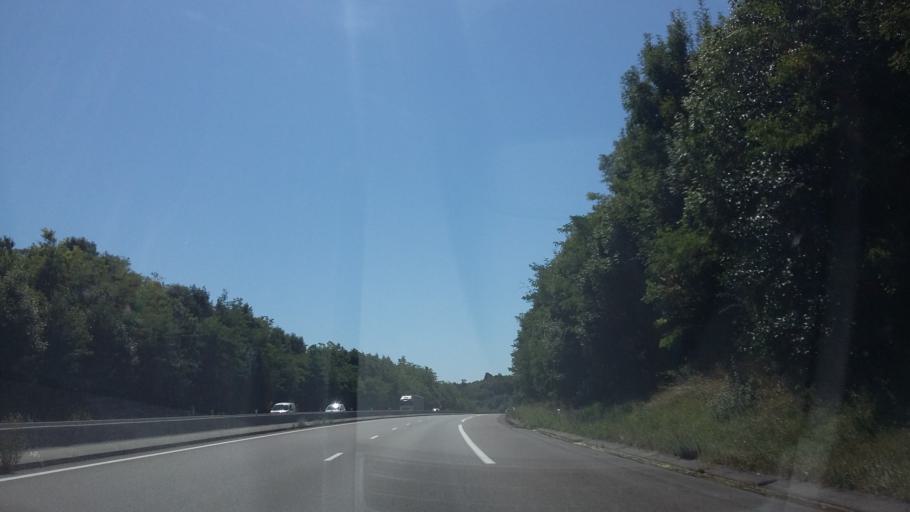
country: FR
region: Rhone-Alpes
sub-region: Departement de l'Isere
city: Chabons
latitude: 45.4538
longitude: 5.4004
